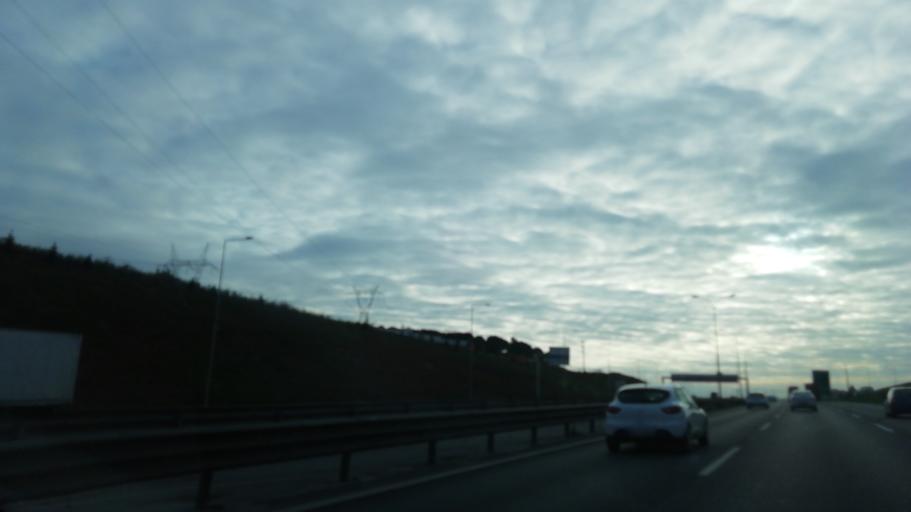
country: TR
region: Istanbul
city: Sultanbeyli
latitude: 40.9461
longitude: 29.3120
